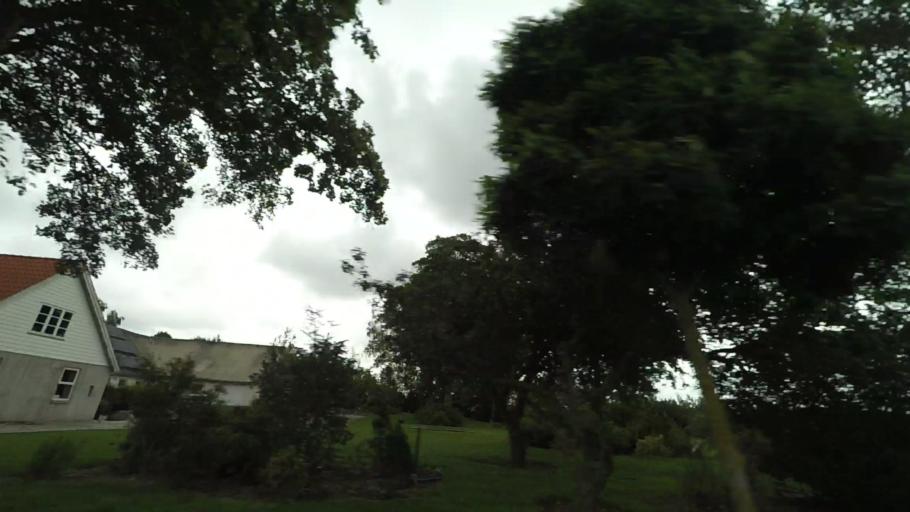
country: DK
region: Central Jutland
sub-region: Syddjurs Kommune
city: Ryomgard
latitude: 56.3895
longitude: 10.5659
